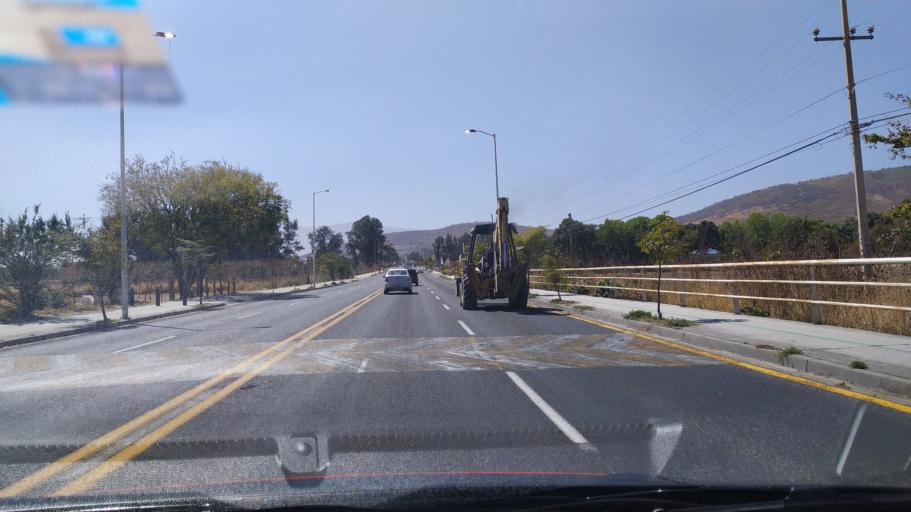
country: MX
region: Jalisco
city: San Sebastian el Grande
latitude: 20.5083
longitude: -103.4133
